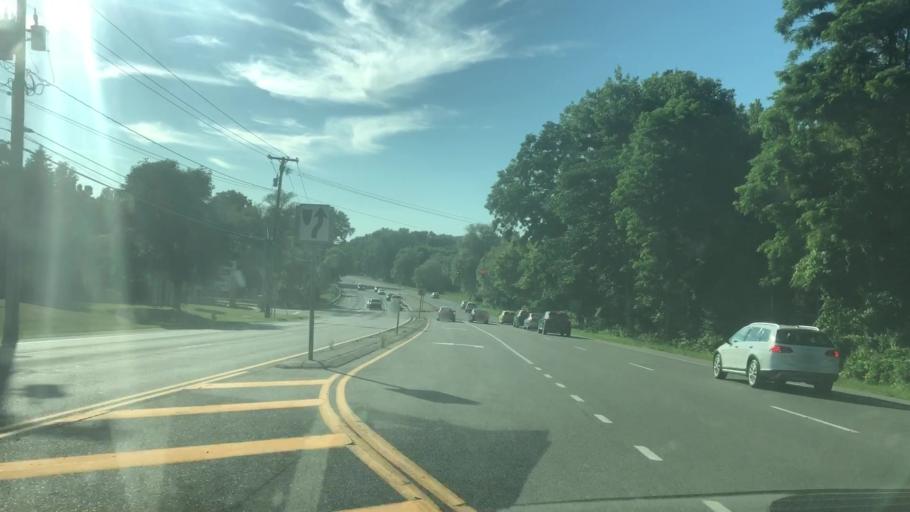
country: US
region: New York
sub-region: Ontario County
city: Victor
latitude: 43.0345
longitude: -77.4447
